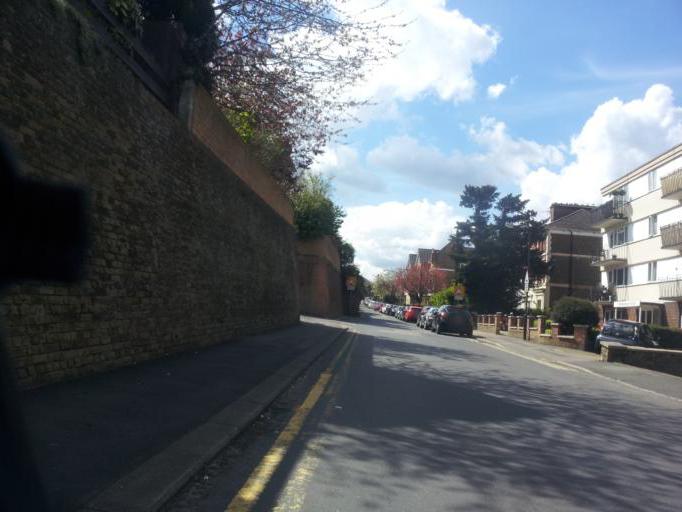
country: GB
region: England
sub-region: Medway
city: Rochester
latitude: 51.3834
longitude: 0.4985
